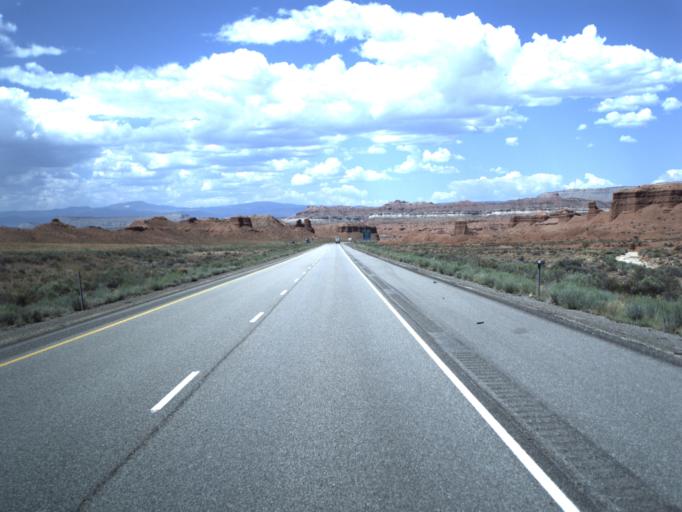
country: US
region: Utah
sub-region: Emery County
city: Ferron
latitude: 38.8469
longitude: -111.0375
